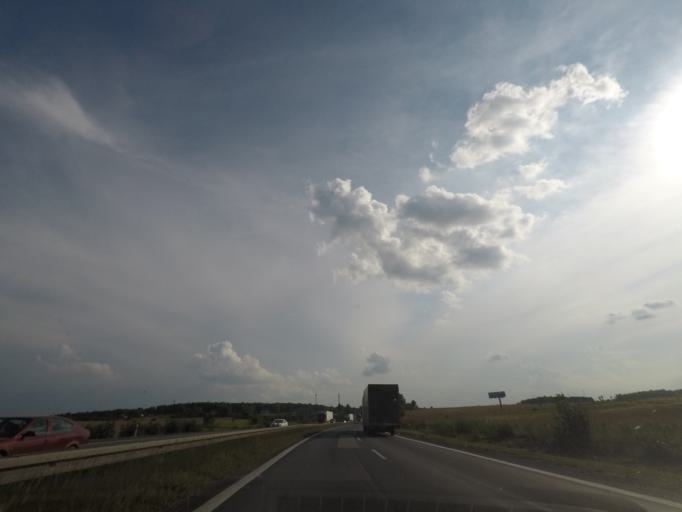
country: PL
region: Silesian Voivodeship
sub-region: Powiat bedzinski
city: Siewierz
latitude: 50.4449
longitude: 19.2230
